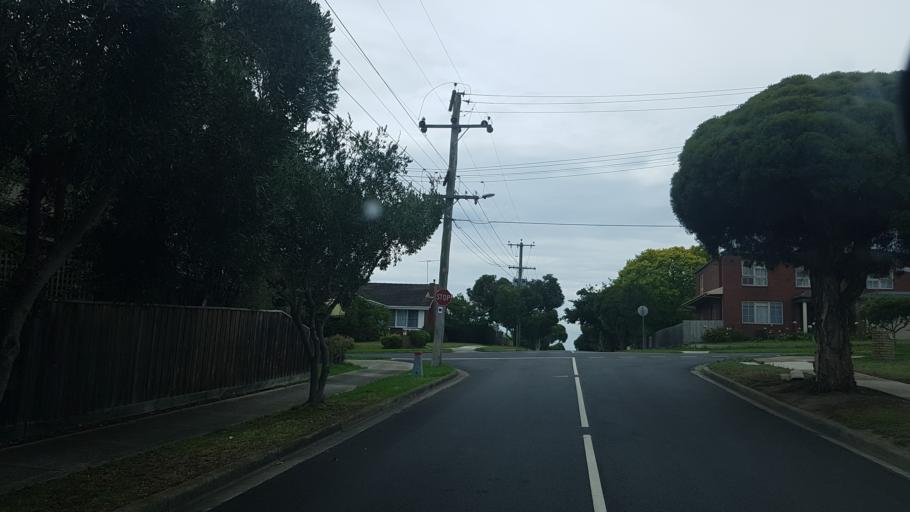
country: AU
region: Victoria
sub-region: Manningham
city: Bulleen
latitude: -37.7606
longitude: 145.0862
